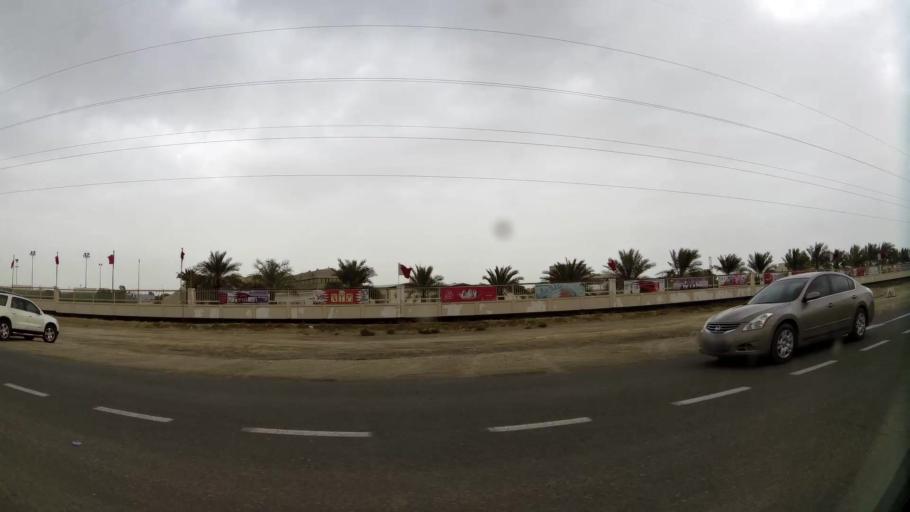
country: BH
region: Northern
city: Madinat `Isa
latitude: 26.1620
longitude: 50.5481
